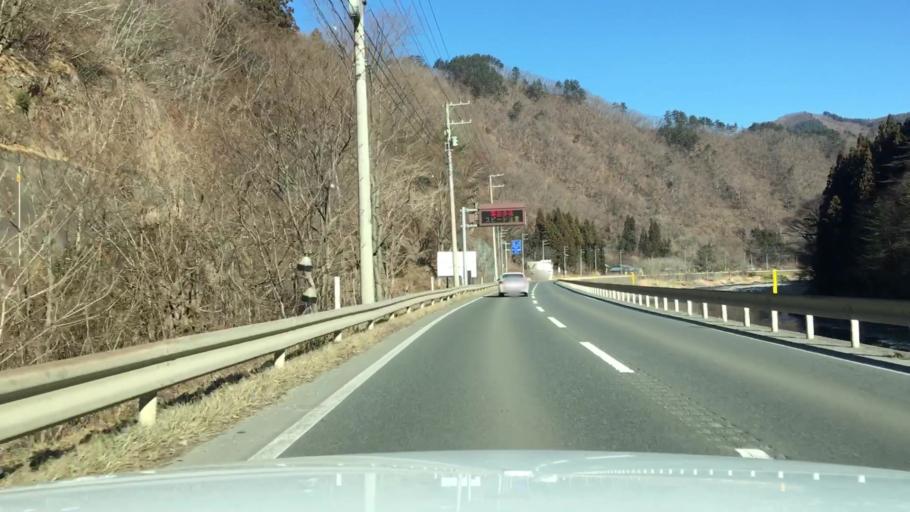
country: JP
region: Iwate
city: Miyako
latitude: 39.6118
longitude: 141.7881
